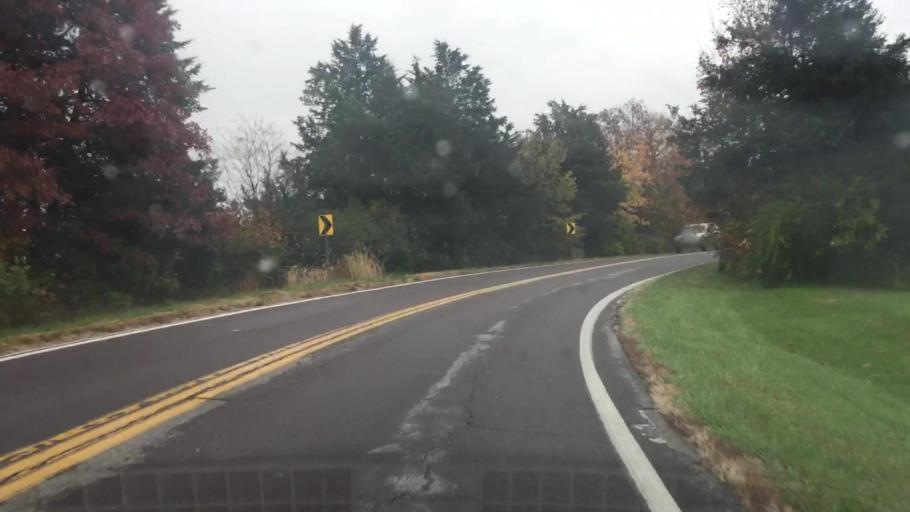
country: US
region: Missouri
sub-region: Callaway County
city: Fulton
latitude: 38.8382
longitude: -91.9206
